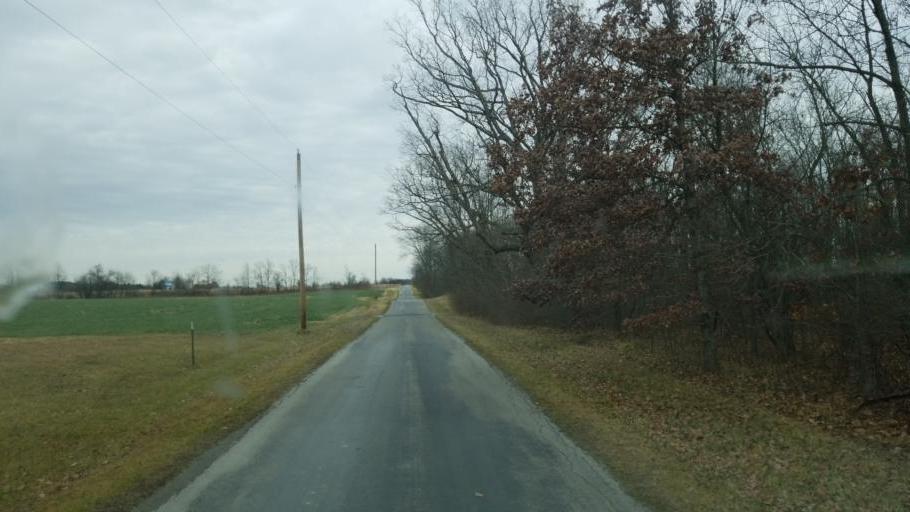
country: US
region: Ohio
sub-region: Hardin County
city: Forest
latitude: 40.7163
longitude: -83.3889
